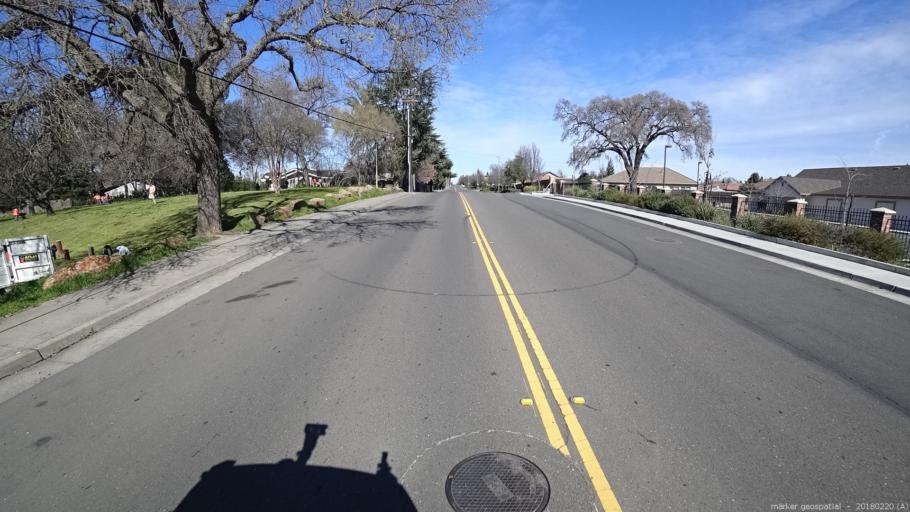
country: US
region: California
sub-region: Sacramento County
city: Orangevale
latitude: 38.6743
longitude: -121.2211
